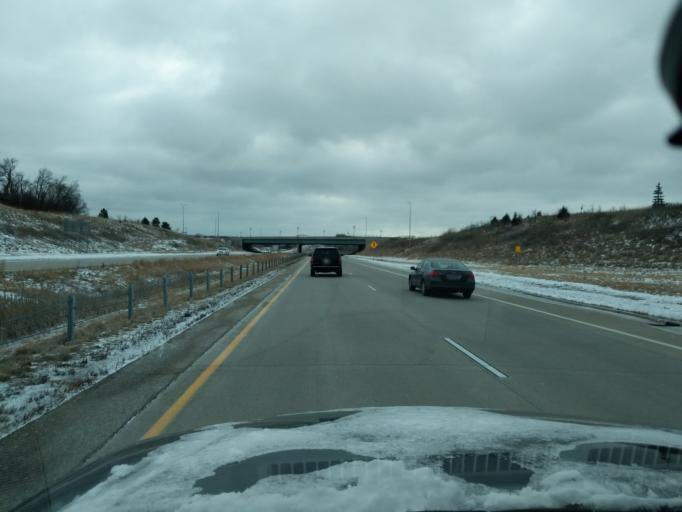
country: US
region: Minnesota
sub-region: Carver County
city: Chanhassen
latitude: 44.8368
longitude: -93.5503
